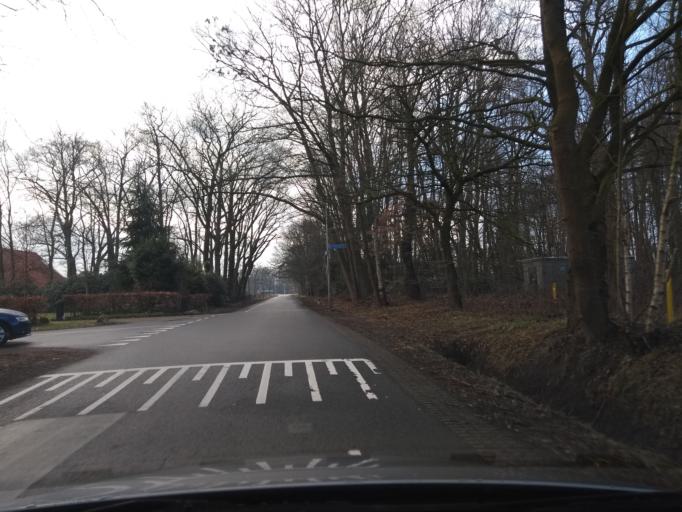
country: NL
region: Overijssel
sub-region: Gemeente Hof van Twente
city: Delden
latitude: 52.2178
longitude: 6.7414
